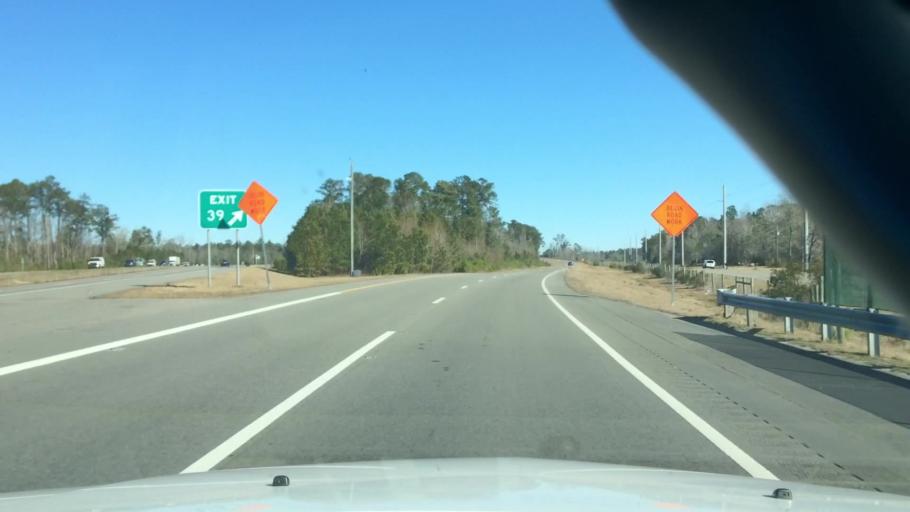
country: US
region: North Carolina
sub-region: Brunswick County
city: Leland
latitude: 34.1829
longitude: -78.0824
